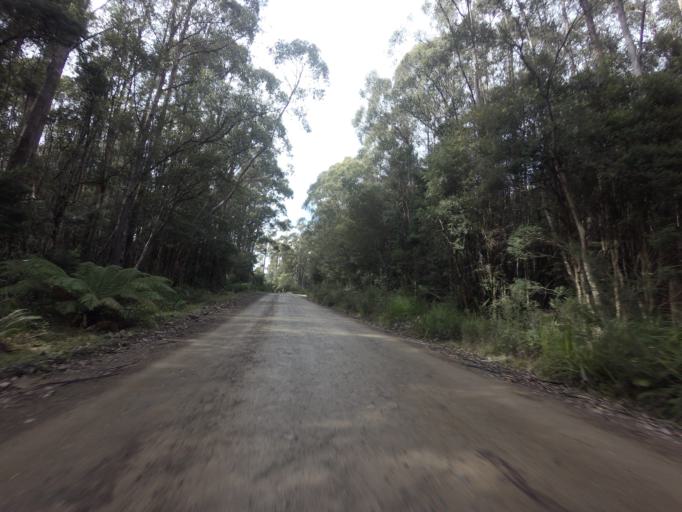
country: AU
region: Tasmania
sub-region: Huon Valley
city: Geeveston
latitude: -43.4815
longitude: 146.8917
